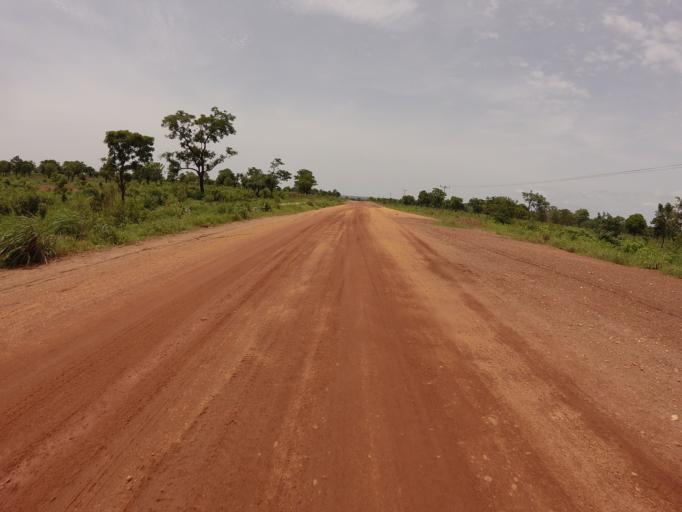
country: GH
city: Kpandae
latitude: 8.7255
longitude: 0.1196
